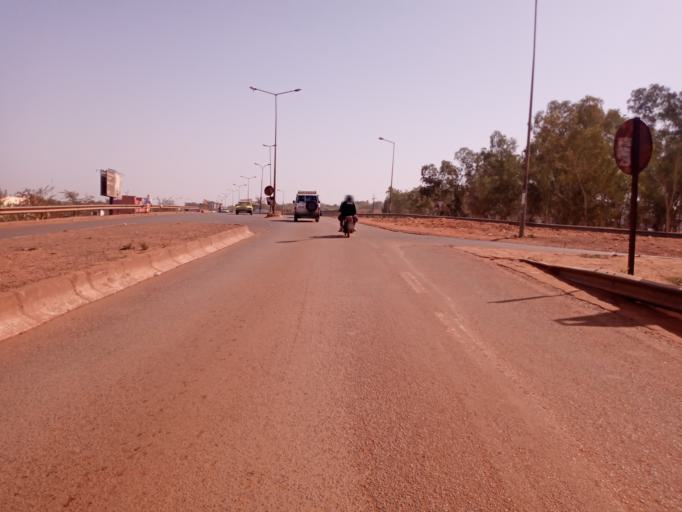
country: ML
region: Bamako
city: Bamako
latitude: 12.6081
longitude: -7.9978
